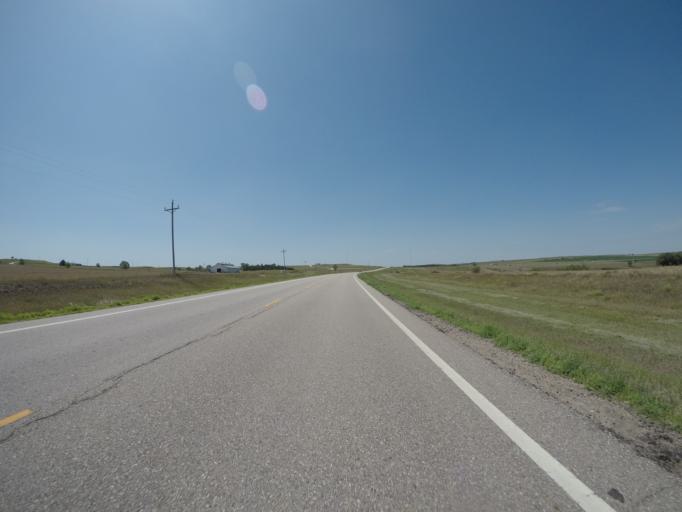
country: US
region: Kansas
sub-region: Osborne County
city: Osborne
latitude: 39.5007
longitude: -98.6936
